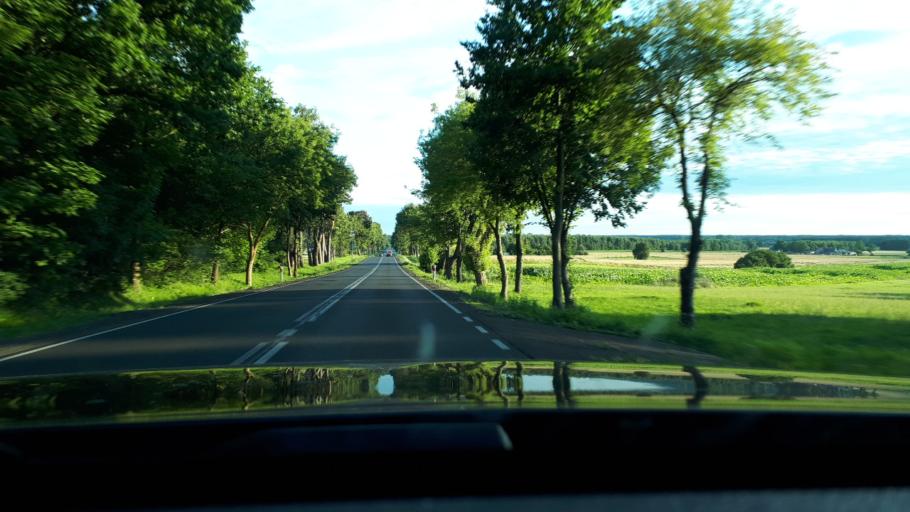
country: PL
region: Masovian Voivodeship
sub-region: Powiat ciechanowski
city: Ojrzen
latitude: 52.7773
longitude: 20.5538
